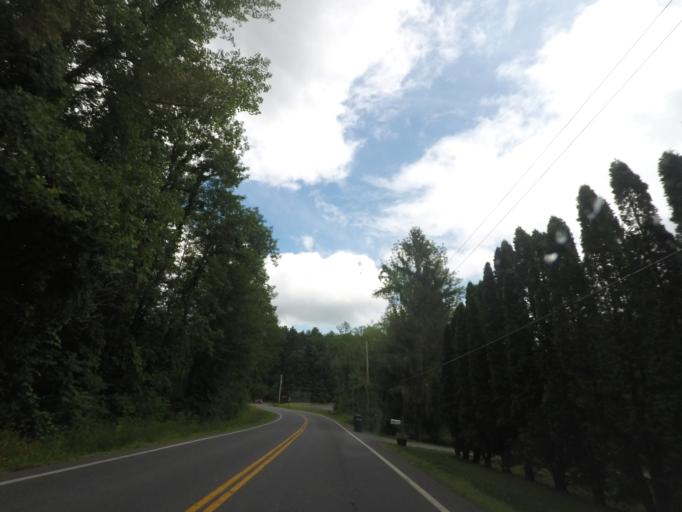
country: US
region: New York
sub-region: Saratoga County
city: Stillwater
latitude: 43.0035
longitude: -73.6980
